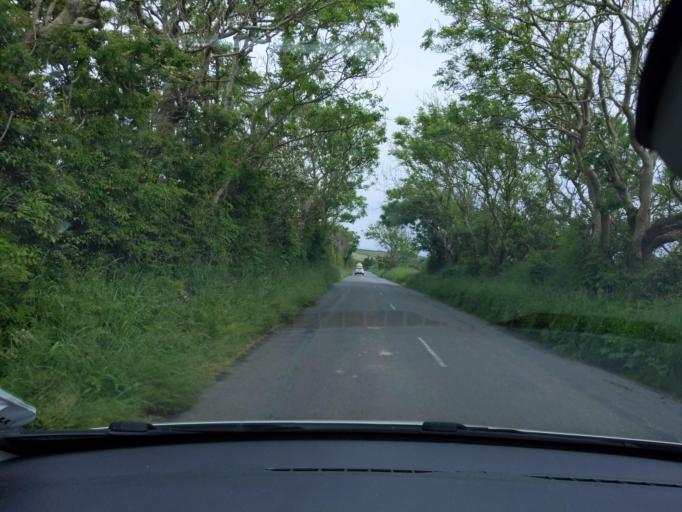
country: IM
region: Douglas
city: Douglas
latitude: 54.1251
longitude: -4.5673
